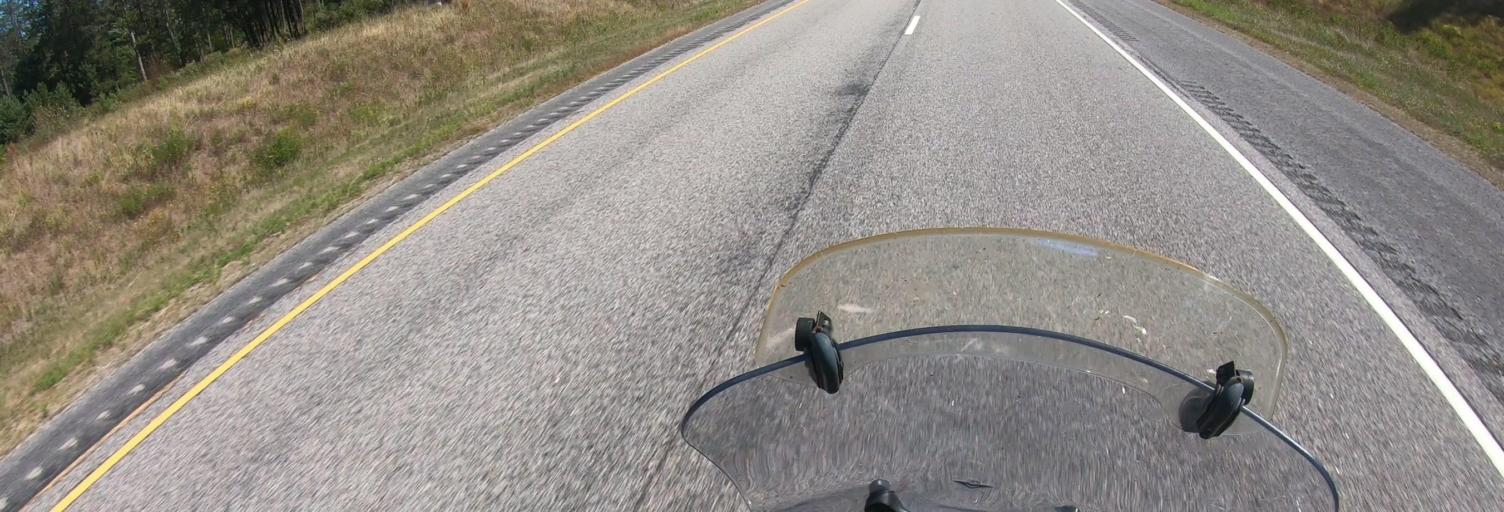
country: US
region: Minnesota
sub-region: Saint Louis County
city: Mountain Iron
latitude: 47.6600
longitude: -92.6043
